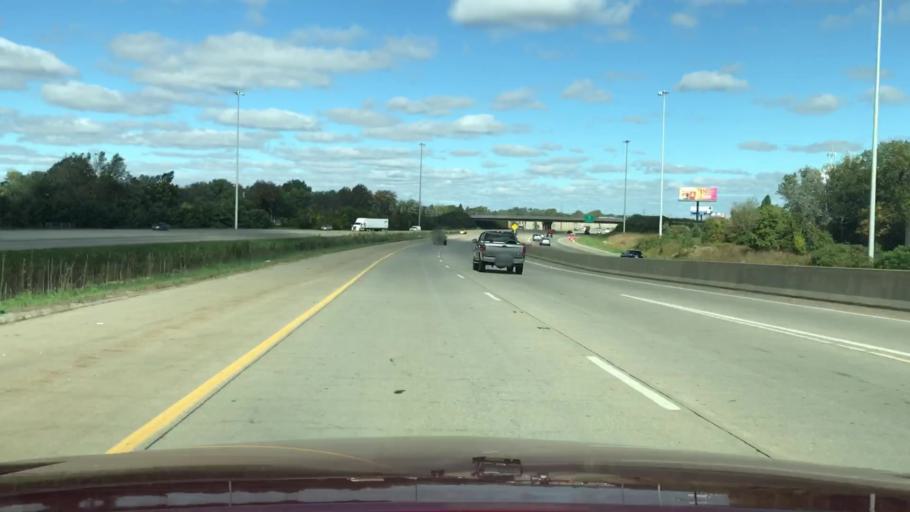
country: US
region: Illinois
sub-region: Cook County
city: Thornton
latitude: 41.5829
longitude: -87.5824
